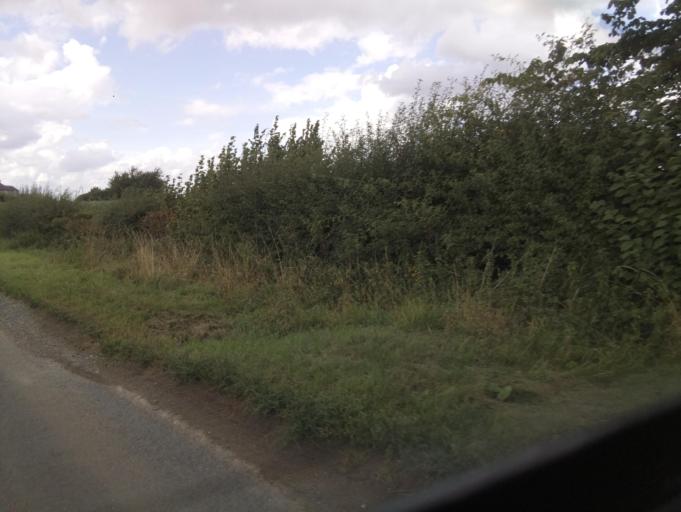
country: GB
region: England
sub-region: North Yorkshire
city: Bedale
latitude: 54.2435
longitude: -1.6894
